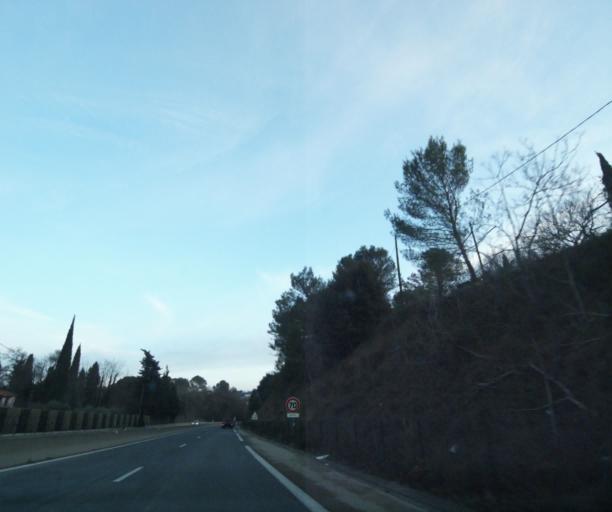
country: FR
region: Provence-Alpes-Cote d'Azur
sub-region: Departement du Var
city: Trans-en-Provence
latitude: 43.4980
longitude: 6.4887
